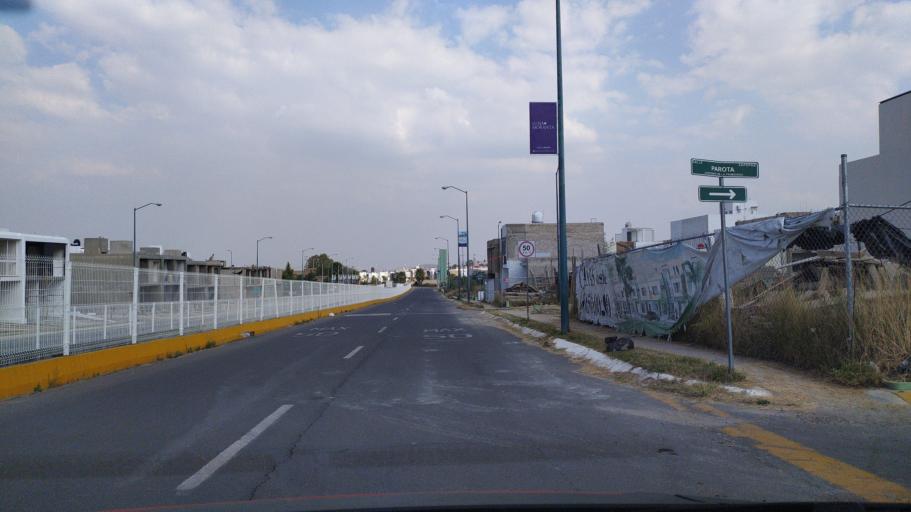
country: MX
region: Jalisco
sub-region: Tlajomulco de Zuniga
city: Palomar
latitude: 20.6317
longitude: -103.4784
